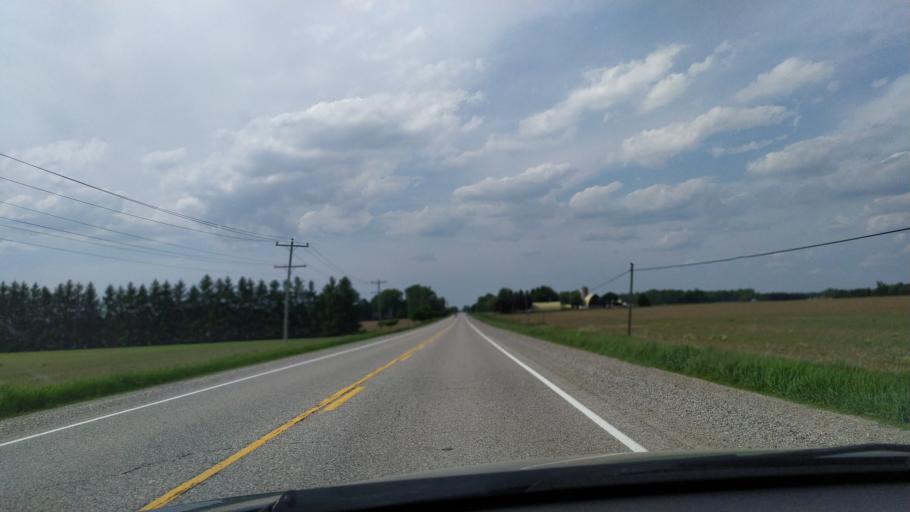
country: CA
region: Ontario
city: Dorchester
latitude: 43.1011
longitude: -81.0108
